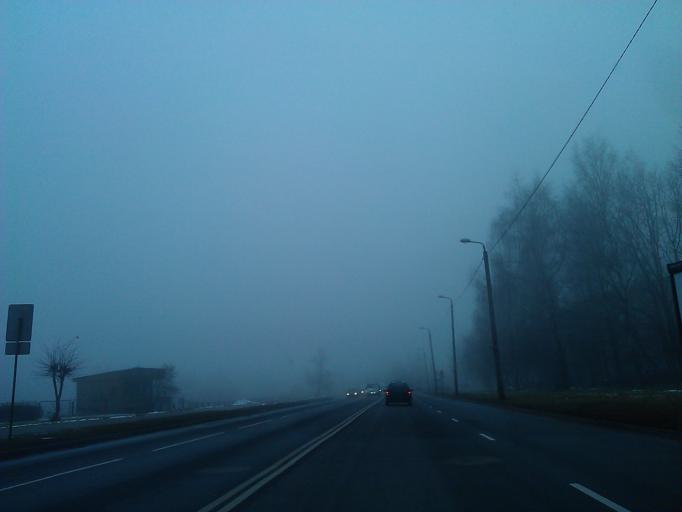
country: LV
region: Riga
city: Bergi
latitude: 56.9779
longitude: 24.2541
